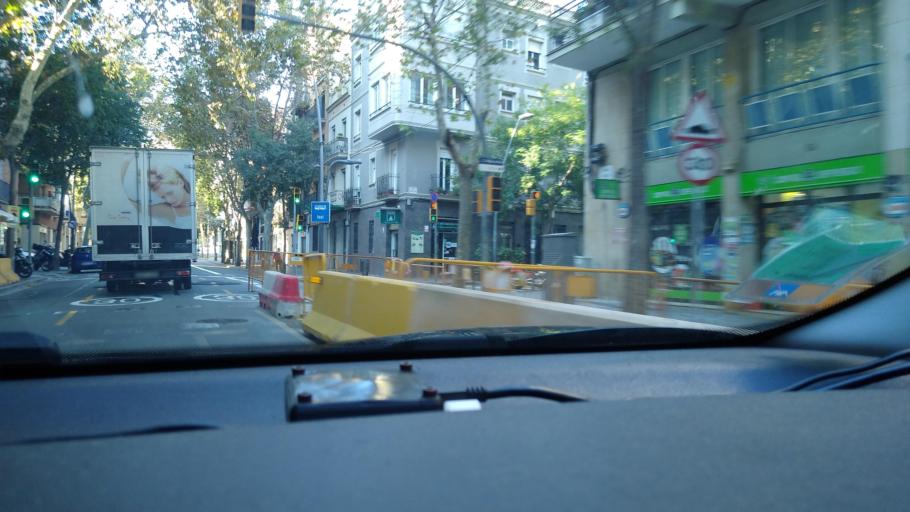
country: ES
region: Catalonia
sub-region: Provincia de Barcelona
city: les Corts
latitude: 41.3779
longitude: 2.1240
